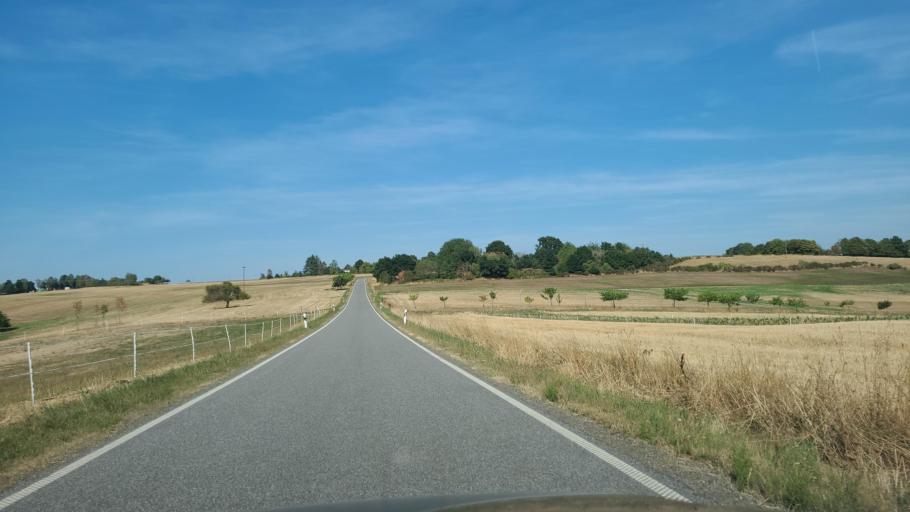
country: DE
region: Rheinland-Pfalz
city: Luckenburg
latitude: 49.7349
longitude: 6.9616
